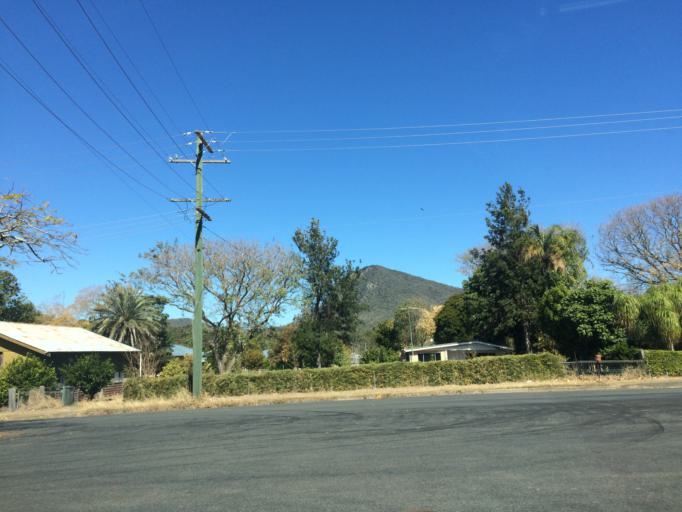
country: AU
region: Queensland
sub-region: Ipswich
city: Thagoona
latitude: -27.9809
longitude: 152.5474
